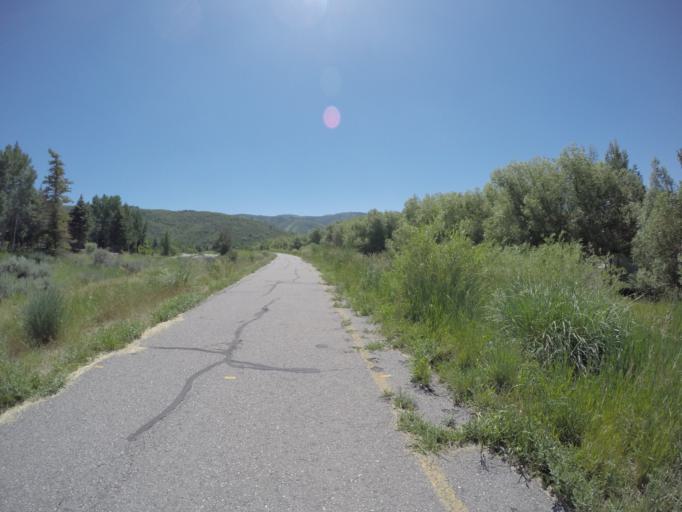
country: US
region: Utah
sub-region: Summit County
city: Park City
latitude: 40.6665
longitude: -111.4853
